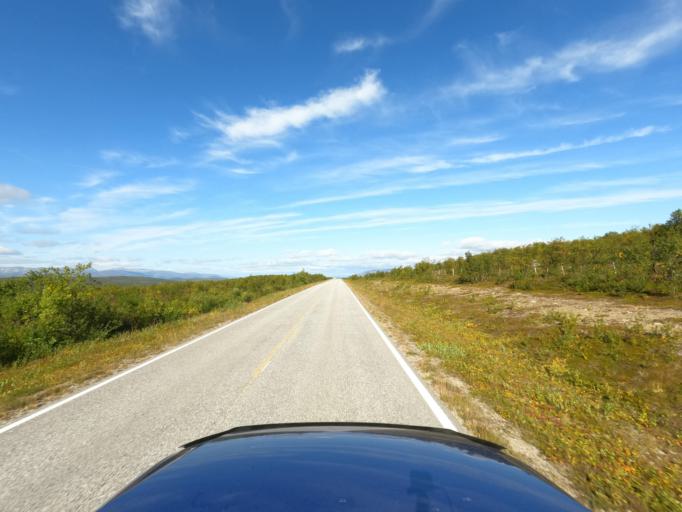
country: NO
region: Finnmark Fylke
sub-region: Karasjok
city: Karasjohka
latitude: 69.7152
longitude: 25.2405
